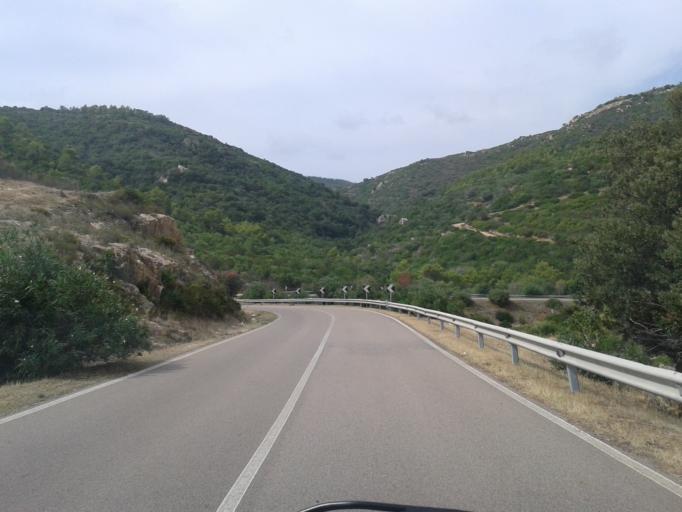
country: IT
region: Sardinia
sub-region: Provincia di Cagliari
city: Villasimius
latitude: 39.1707
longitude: 9.5598
